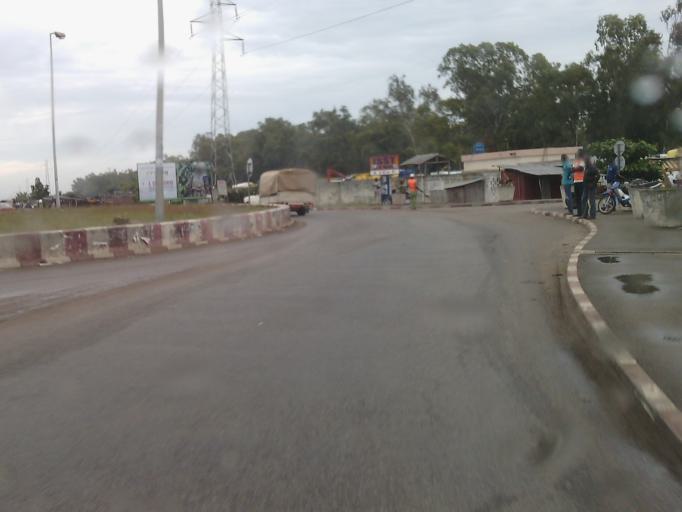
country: BJ
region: Queme
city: Porto-Novo
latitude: 6.3744
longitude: 2.5625
